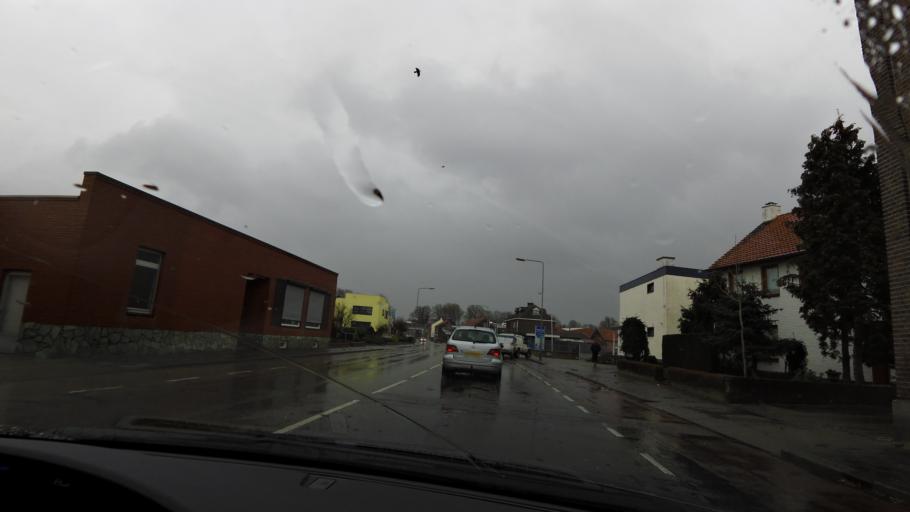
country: NL
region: Limburg
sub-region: Gemeente Beek
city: Beek
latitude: 50.9453
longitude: 5.7845
